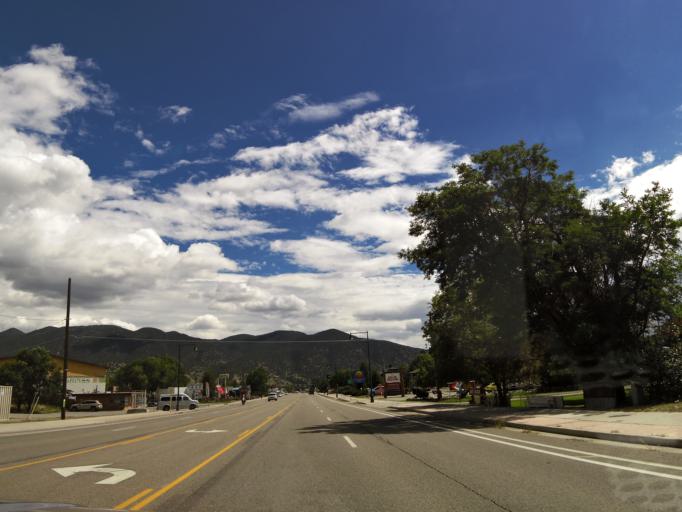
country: US
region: Colorado
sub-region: Chaffee County
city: Salida
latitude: 38.5241
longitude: -106.0015
